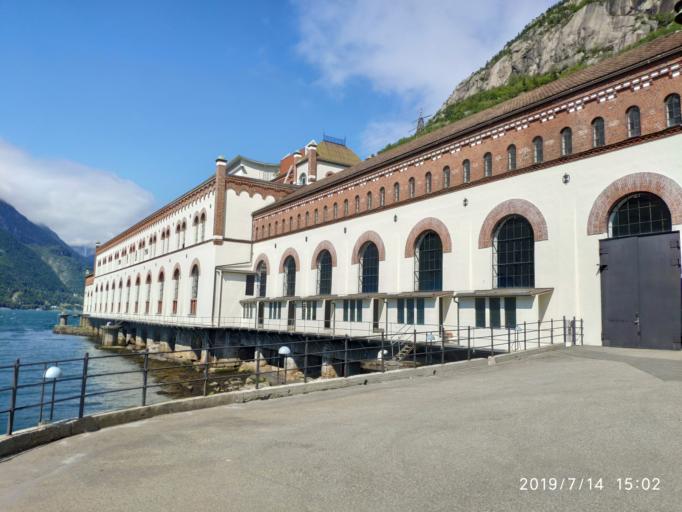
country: NO
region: Hordaland
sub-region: Odda
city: Odda
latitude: 60.1209
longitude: 6.5560
